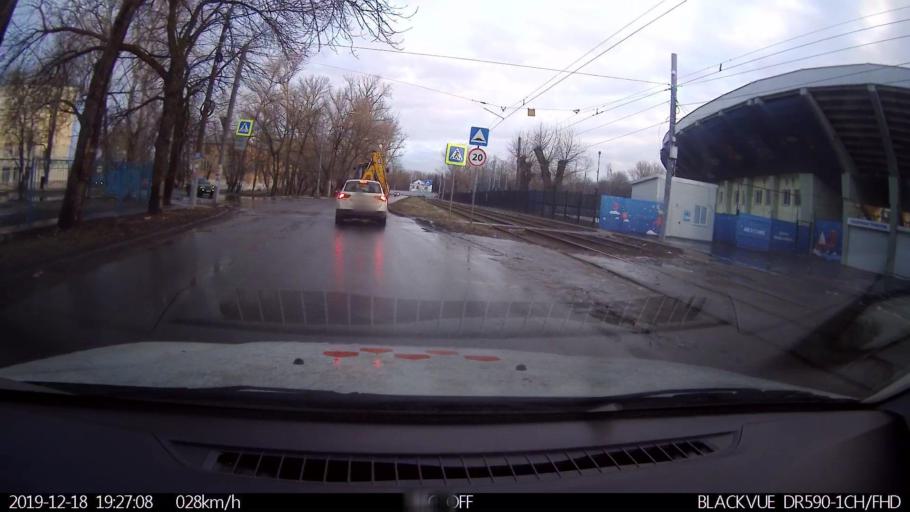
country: RU
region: Nizjnij Novgorod
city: Nizhniy Novgorod
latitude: 56.3102
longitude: 43.9275
